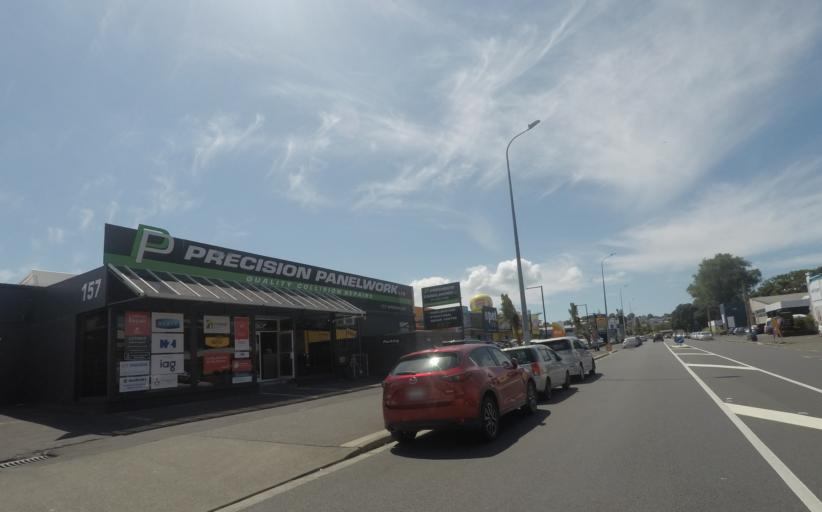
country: NZ
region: Auckland
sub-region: Auckland
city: Tamaki
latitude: -36.8753
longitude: 174.8540
